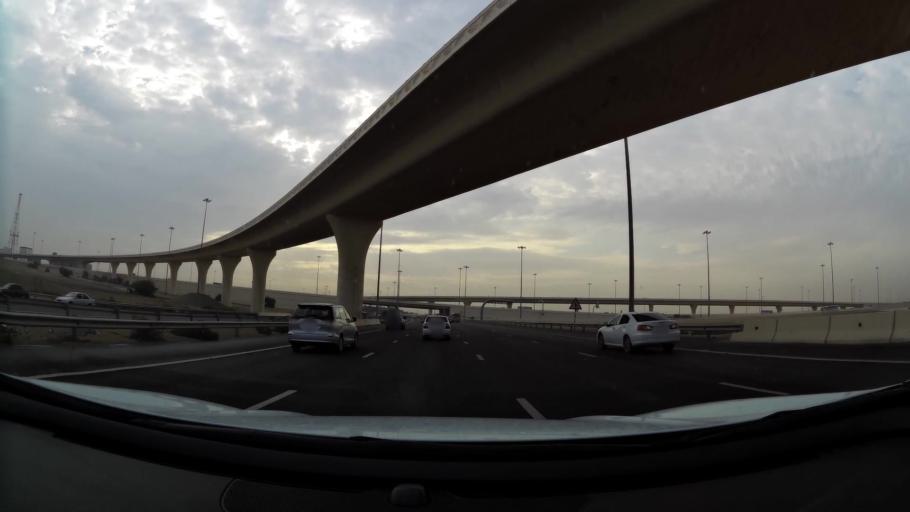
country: AE
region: Abu Dhabi
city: Abu Dhabi
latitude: 24.3105
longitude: 54.5985
